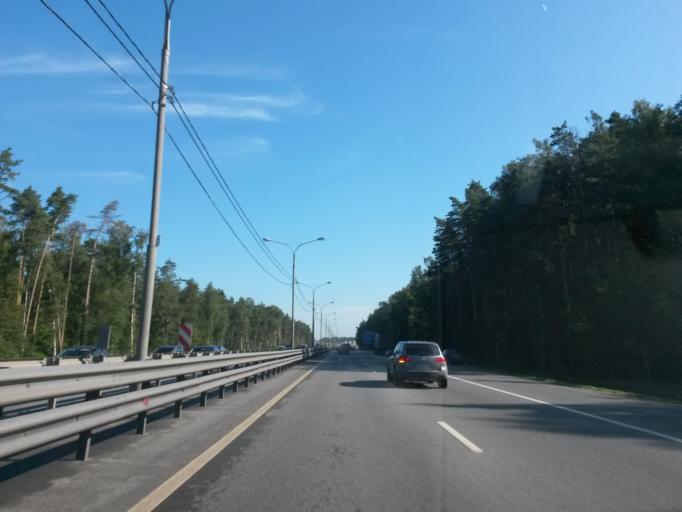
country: RU
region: Moskovskaya
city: Kostino
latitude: 56.0358
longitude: 37.8899
